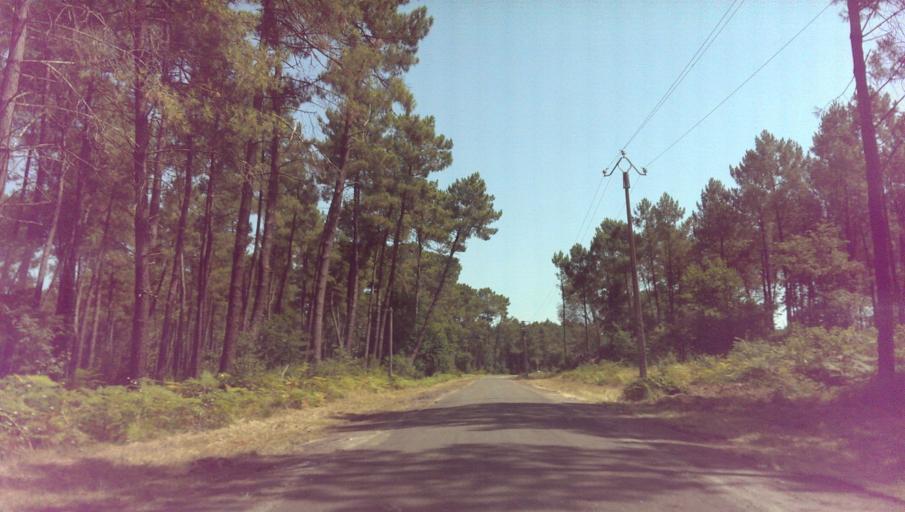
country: FR
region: Aquitaine
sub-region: Departement des Landes
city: Sarbazan
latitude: 44.0647
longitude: -0.1653
